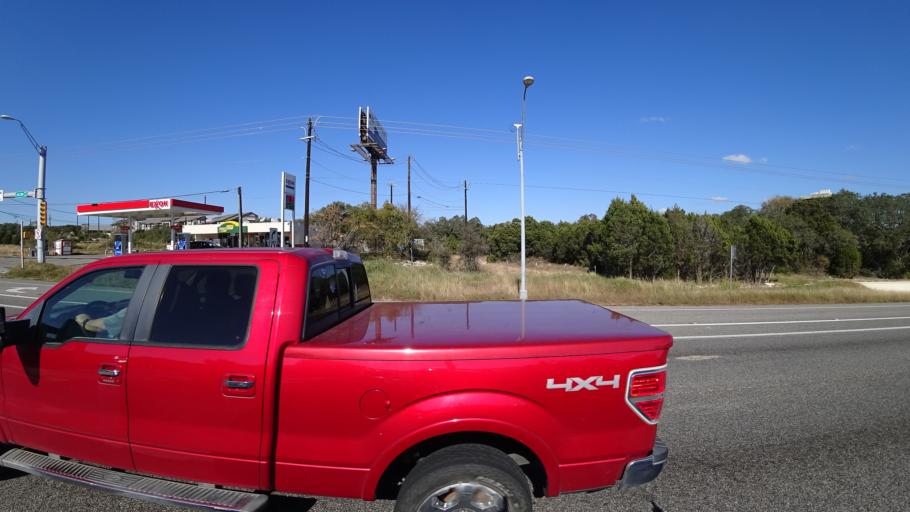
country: US
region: Texas
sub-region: Travis County
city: Barton Creek
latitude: 30.2292
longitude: -97.8877
